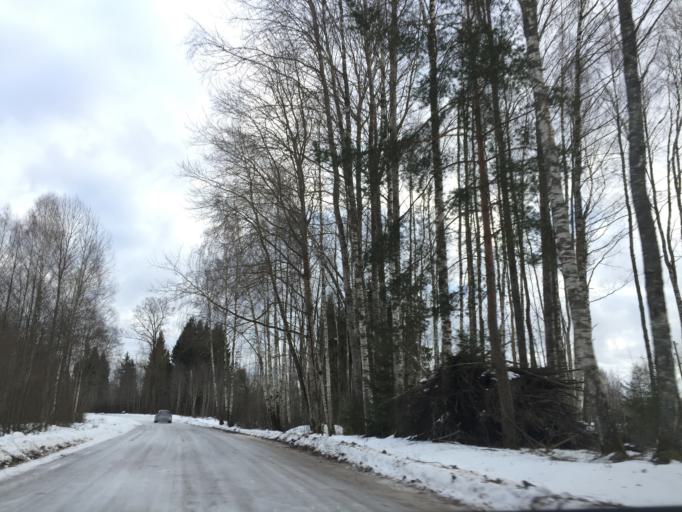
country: LV
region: Lielvarde
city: Lielvarde
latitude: 56.5809
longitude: 24.7627
